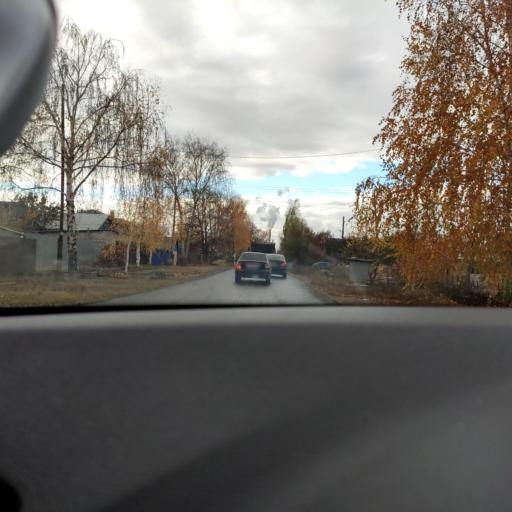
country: RU
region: Samara
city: Petra-Dubrava
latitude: 53.2486
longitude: 50.3215
